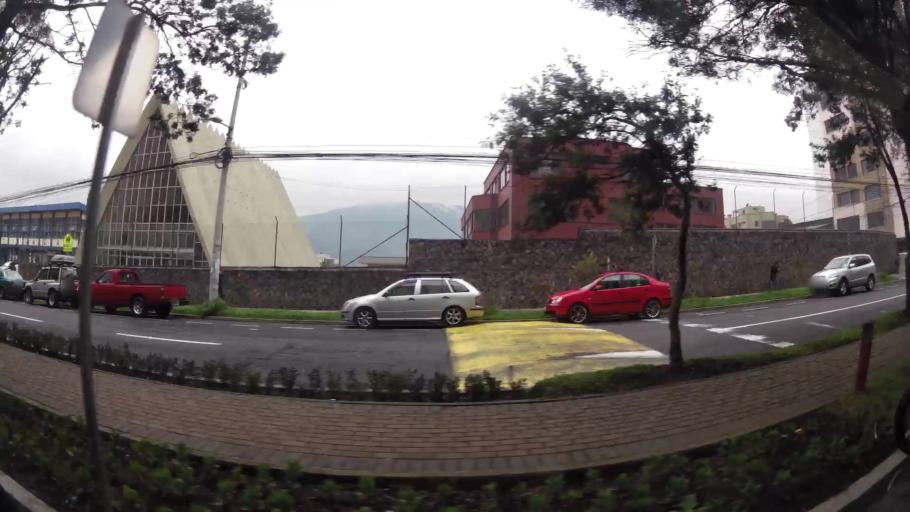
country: EC
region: Pichincha
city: Quito
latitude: -0.1987
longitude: -78.4794
